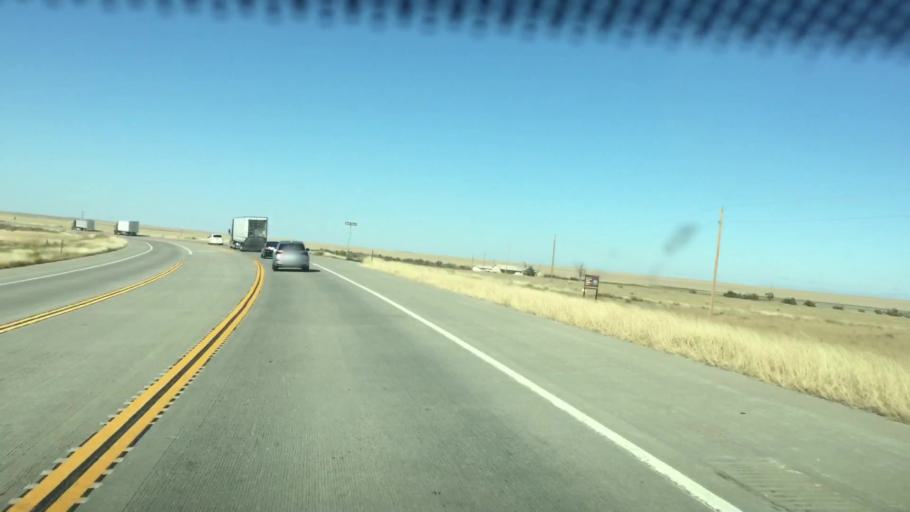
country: US
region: Colorado
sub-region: Kiowa County
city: Eads
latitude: 38.3471
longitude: -102.7147
